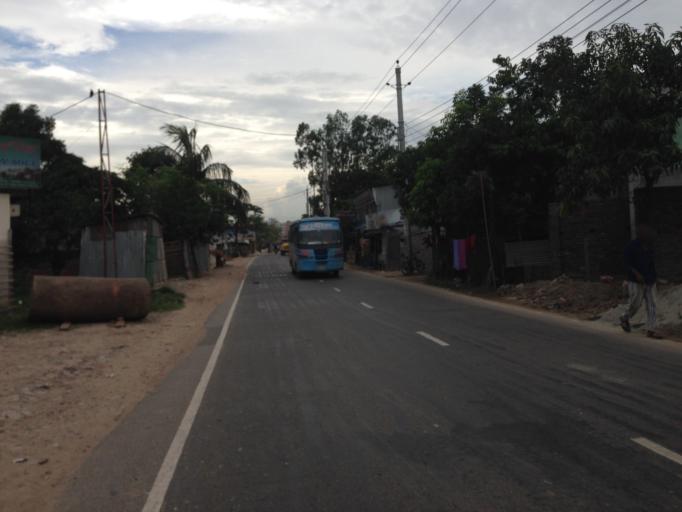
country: BD
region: Dhaka
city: Paltan
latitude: 23.7537
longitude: 90.4511
